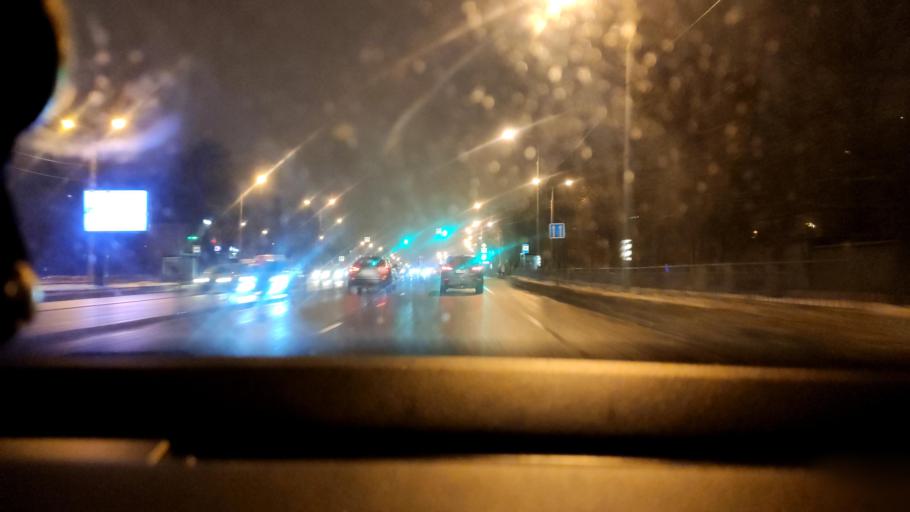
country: RU
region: Moskovskaya
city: Sergiyev Posad
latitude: 56.2860
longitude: 38.1255
